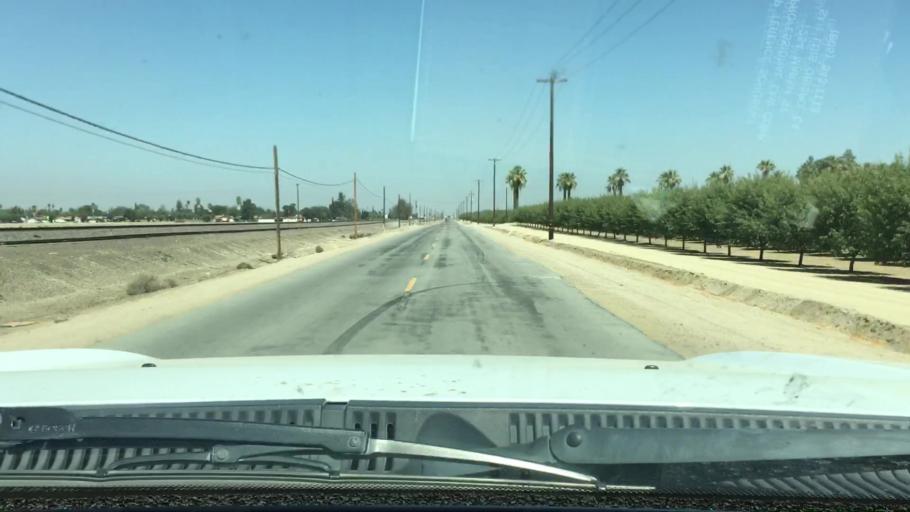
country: US
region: California
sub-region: Kern County
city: Wasco
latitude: 35.5674
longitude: -119.3318
